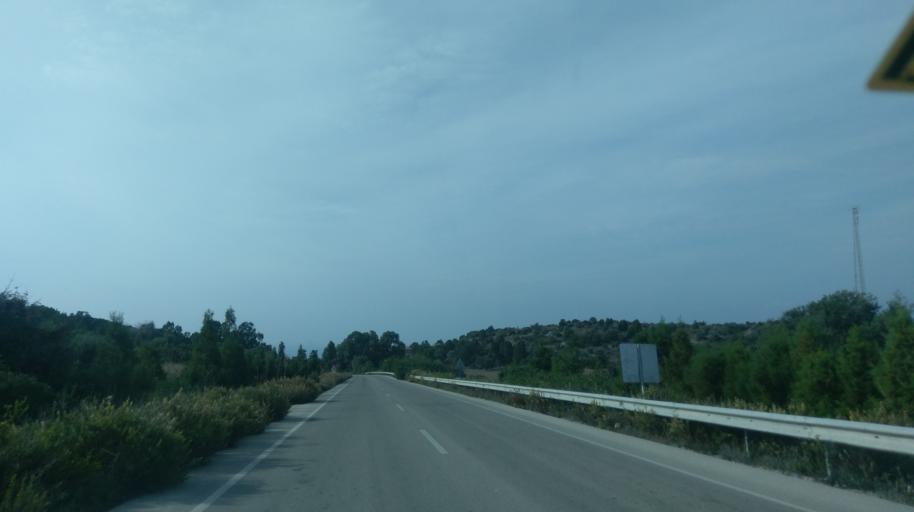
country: CY
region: Ammochostos
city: Trikomo
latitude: 35.4289
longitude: 33.9763
